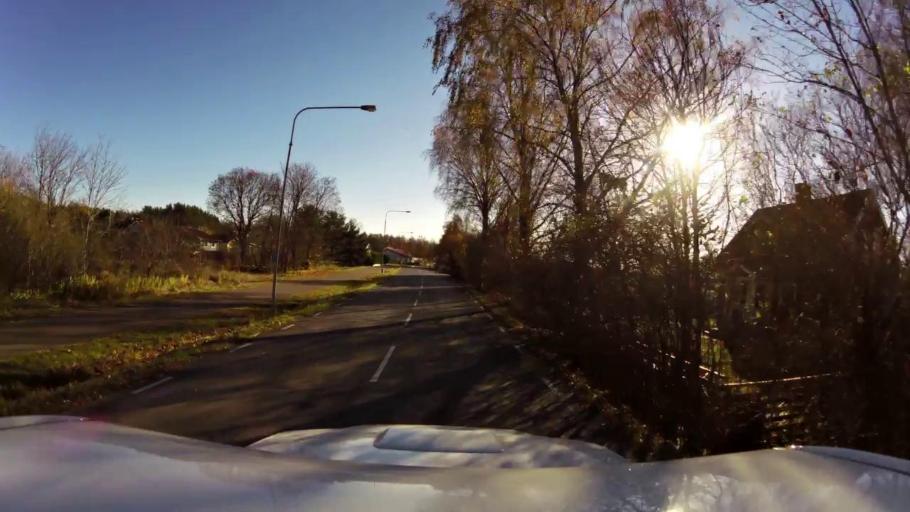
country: SE
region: OEstergoetland
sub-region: Linkopings Kommun
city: Malmslatt
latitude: 58.3627
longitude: 15.5615
